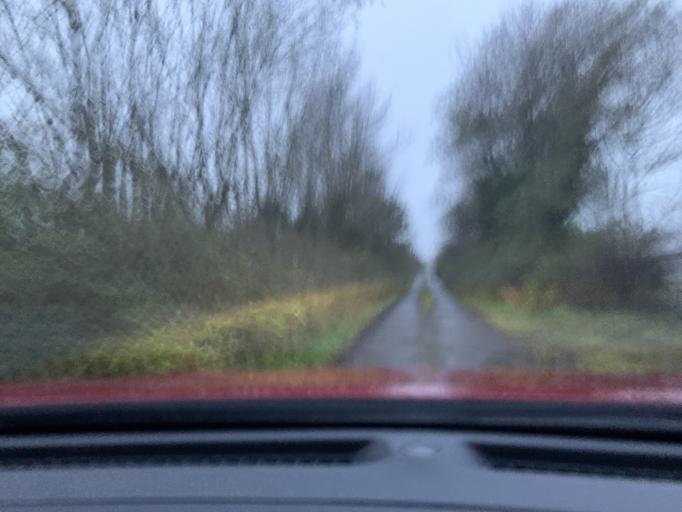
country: IE
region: Connaught
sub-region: Sligo
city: Ballymote
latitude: 54.0186
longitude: -8.5301
